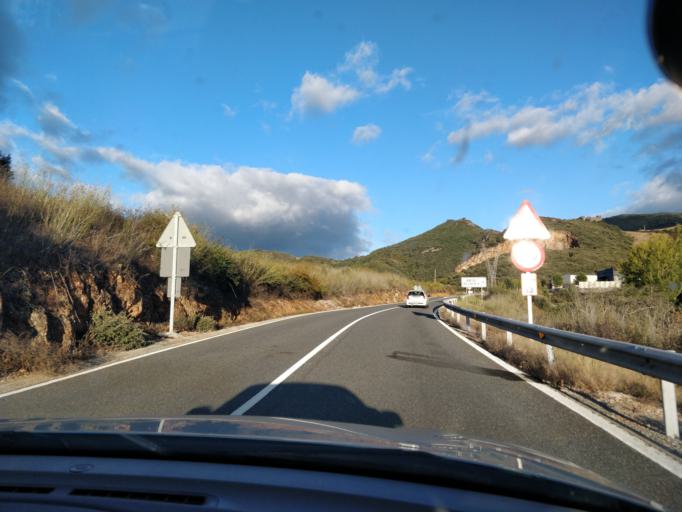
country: ES
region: Castille and Leon
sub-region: Provincia de Leon
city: Borrenes
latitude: 42.4919
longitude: -6.7053
